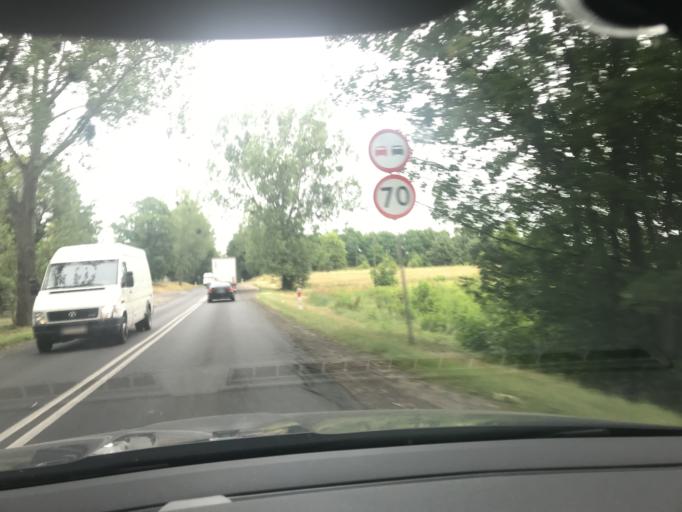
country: PL
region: Lodz Voivodeship
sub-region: Powiat zgierski
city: Zgierz
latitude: 51.8961
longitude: 19.4231
